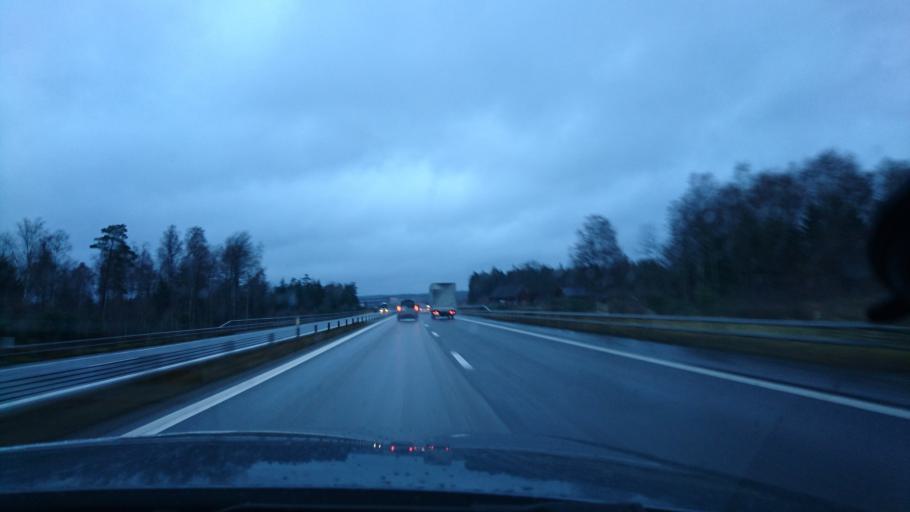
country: SE
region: Kronoberg
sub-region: Markaryds Kommun
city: Markaryd
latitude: 56.4613
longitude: 13.6271
